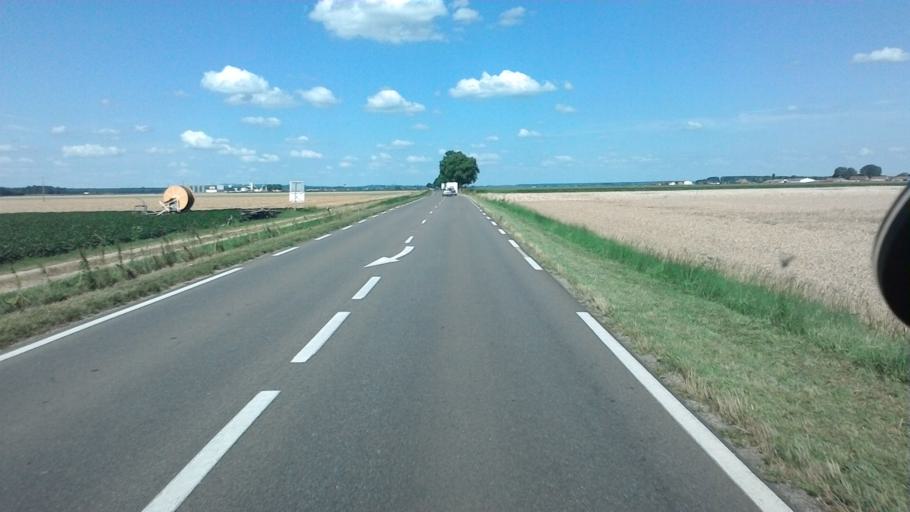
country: FR
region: Franche-Comte
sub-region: Departement du Jura
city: Saint-Aubin
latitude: 47.0060
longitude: 5.3593
